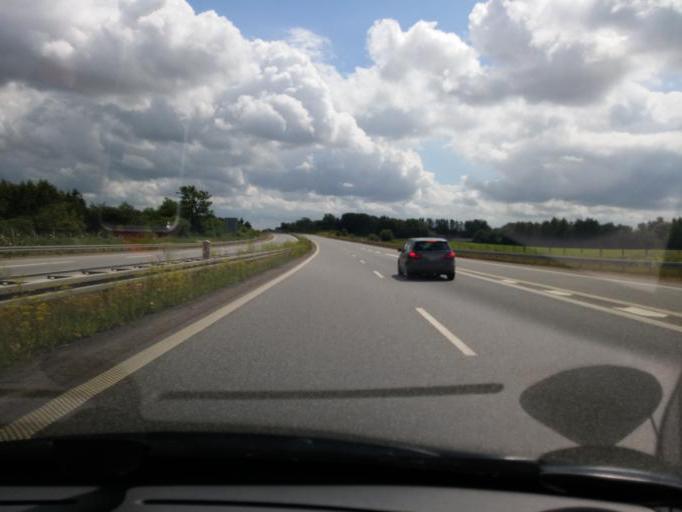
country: DK
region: South Denmark
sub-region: Faaborg-Midtfyn Kommune
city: Ringe
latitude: 55.2160
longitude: 10.5030
